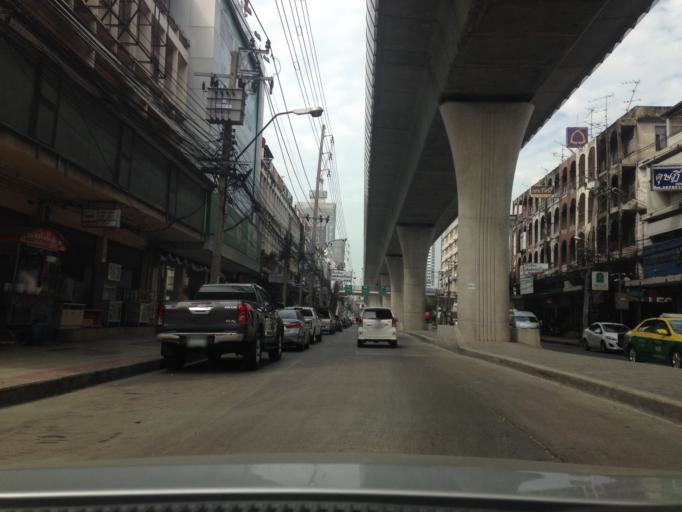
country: TH
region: Bangkok
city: Bang Sue
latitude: 13.8065
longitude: 100.5266
